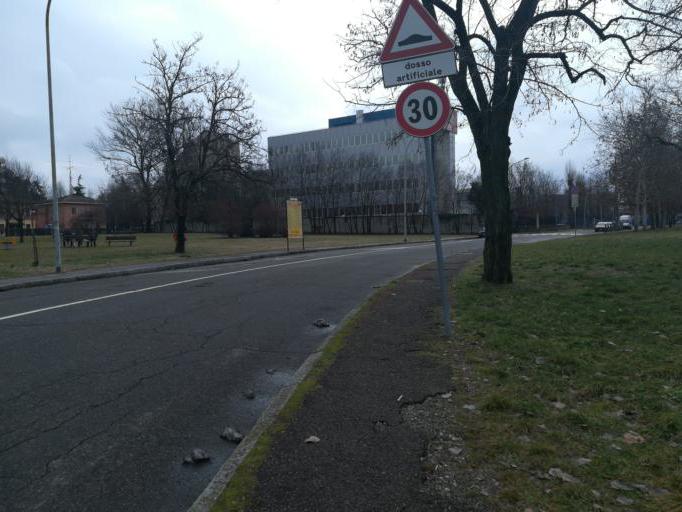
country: IT
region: Emilia-Romagna
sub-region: Provincia di Bologna
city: Progresso
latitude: 44.5409
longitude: 11.3548
